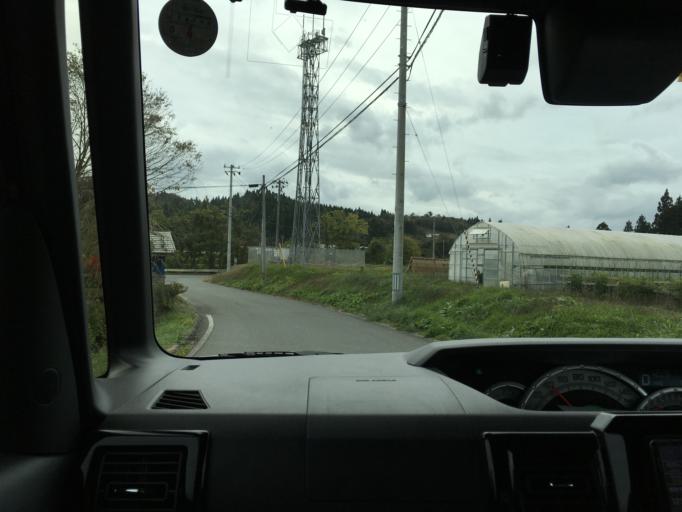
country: JP
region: Iwate
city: Ichinoseki
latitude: 39.0185
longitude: 141.3478
